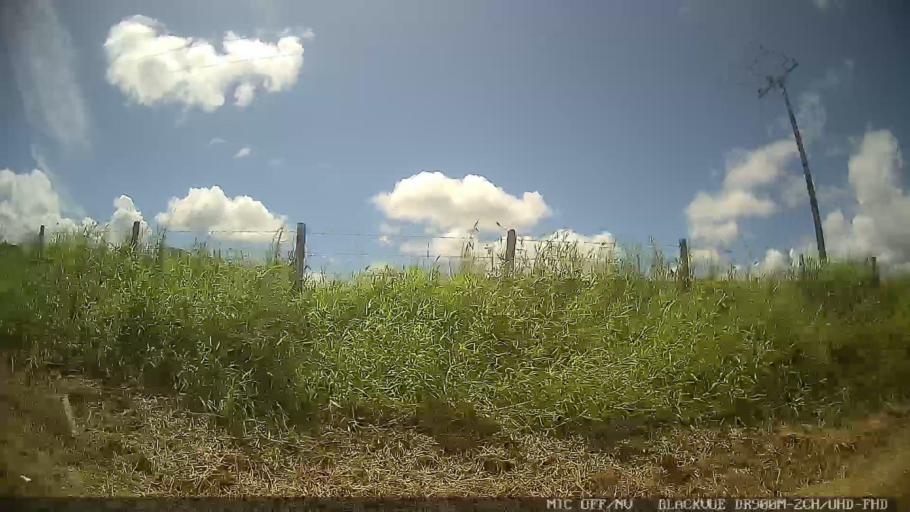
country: BR
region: Sao Paulo
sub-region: Amparo
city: Amparo
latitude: -22.8235
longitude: -46.6991
